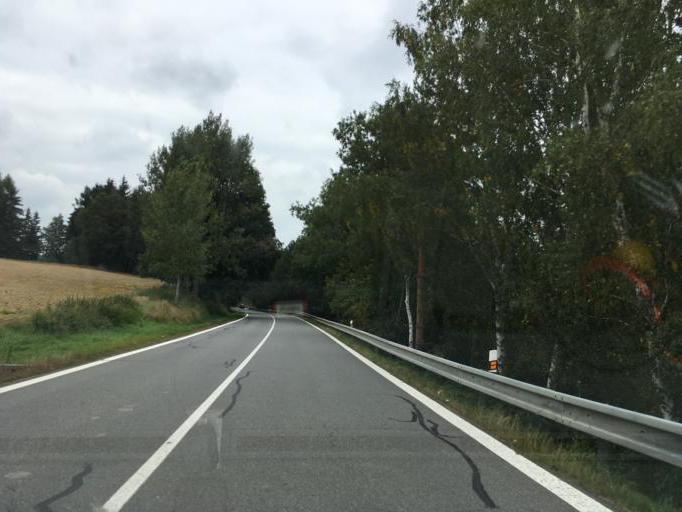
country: CZ
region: Central Bohemia
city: Cechtice
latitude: 49.5765
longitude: 15.0951
